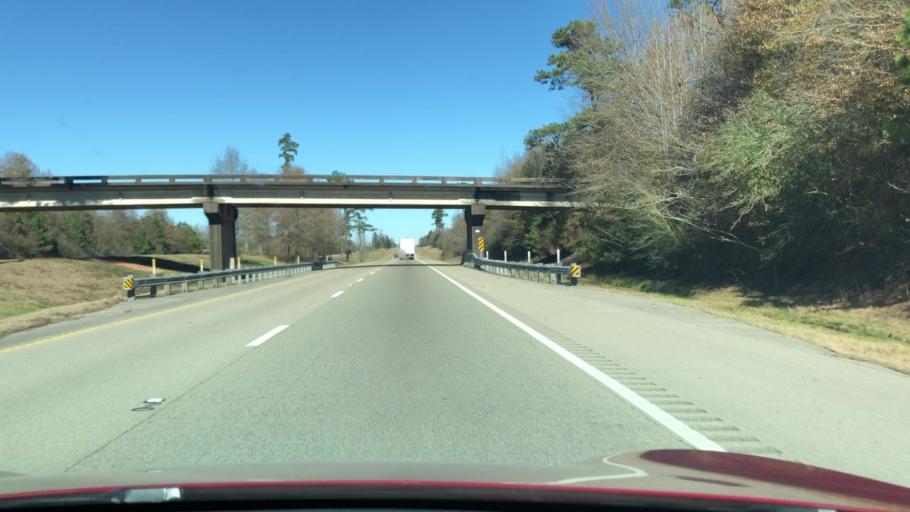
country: US
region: Mississippi
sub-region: Pearl River County
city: Poplarville
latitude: 30.7640
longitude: -89.5212
